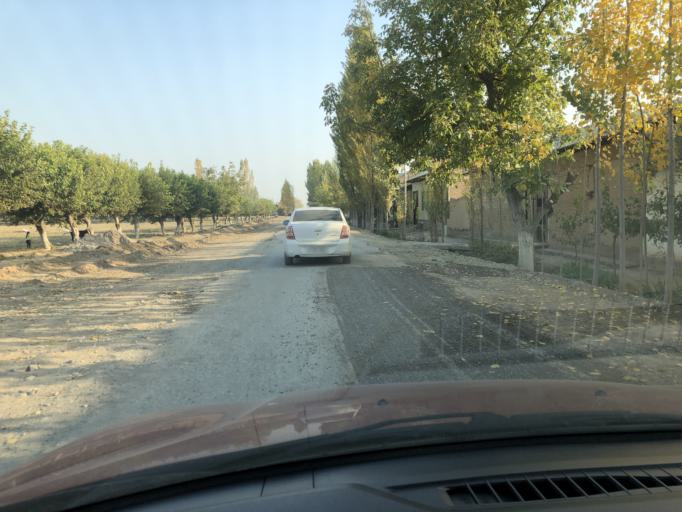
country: UZ
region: Namangan
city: Uychi
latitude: 41.0654
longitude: 71.9864
